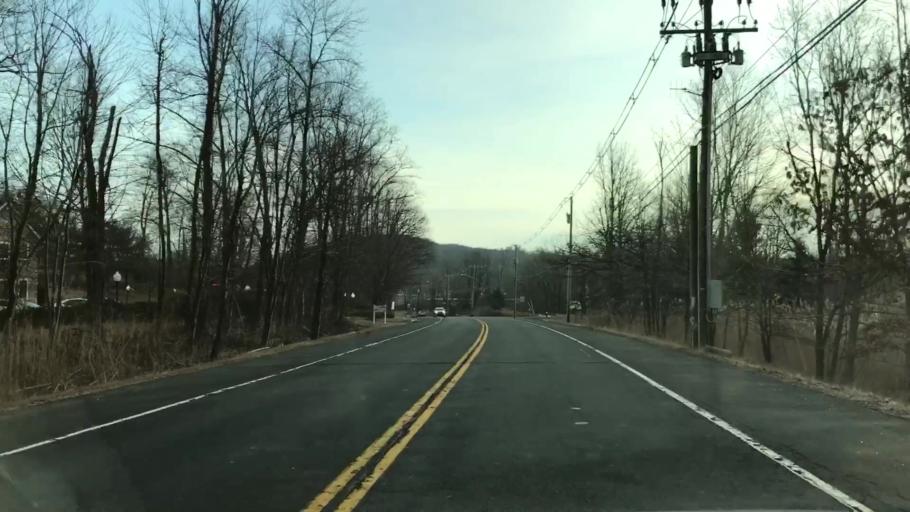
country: US
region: New York
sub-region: Rockland County
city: Pomona
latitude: 41.1821
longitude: -74.0537
